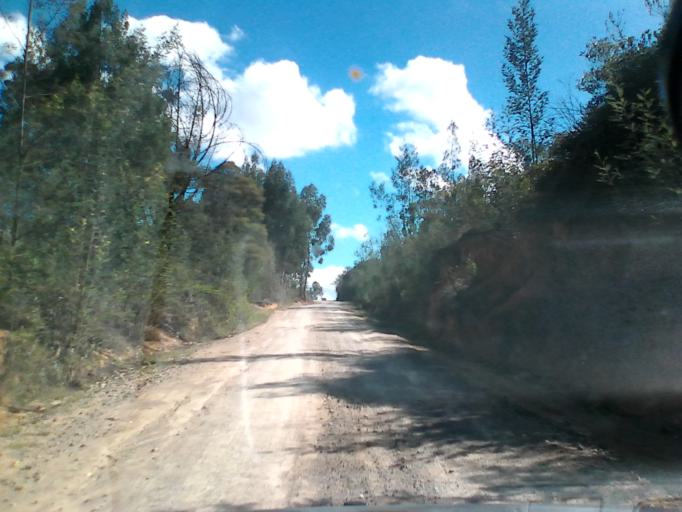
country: CO
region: Boyaca
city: Tibasosa
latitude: 5.7786
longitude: -73.0243
